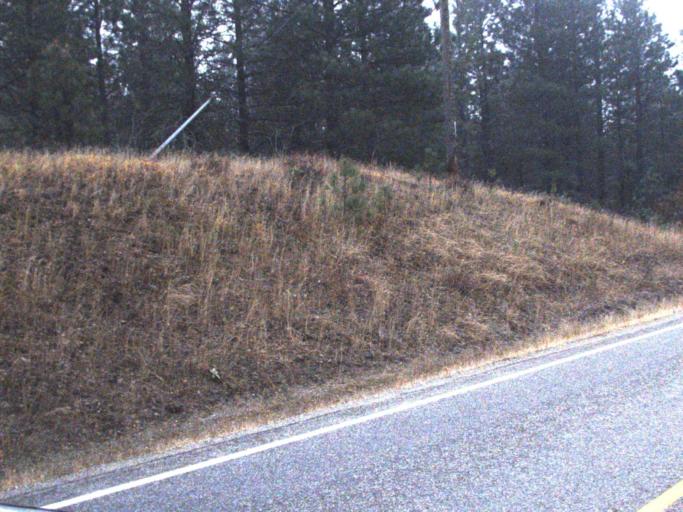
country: CA
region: British Columbia
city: Grand Forks
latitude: 48.9965
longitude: -118.2248
